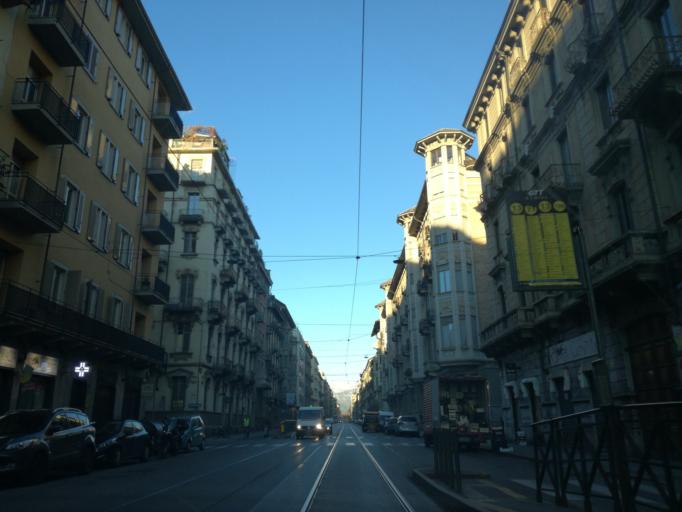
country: IT
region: Piedmont
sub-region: Provincia di Torino
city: Turin
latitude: 45.0785
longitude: 7.6644
